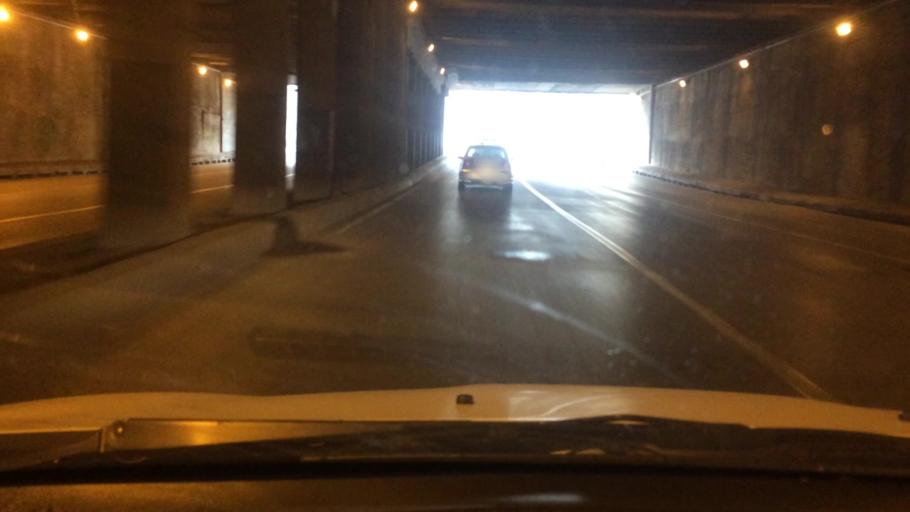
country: GE
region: T'bilisi
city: Tbilisi
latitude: 41.7133
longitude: 44.7826
